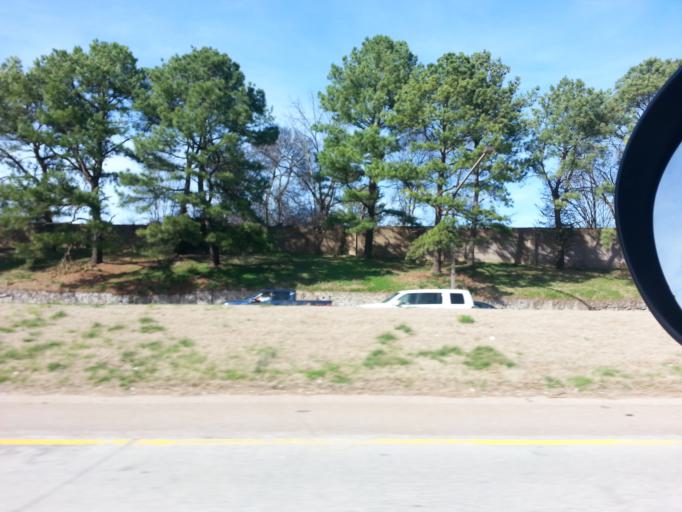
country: US
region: Tennessee
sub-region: Davidson County
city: Oak Hill
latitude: 36.1242
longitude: -86.7443
